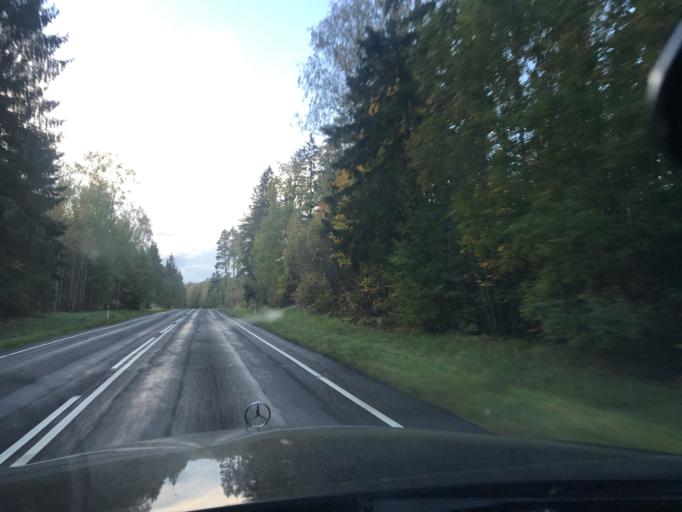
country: EE
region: Vorumaa
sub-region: Antsla vald
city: Vana-Antsla
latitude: 57.8769
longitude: 26.5841
